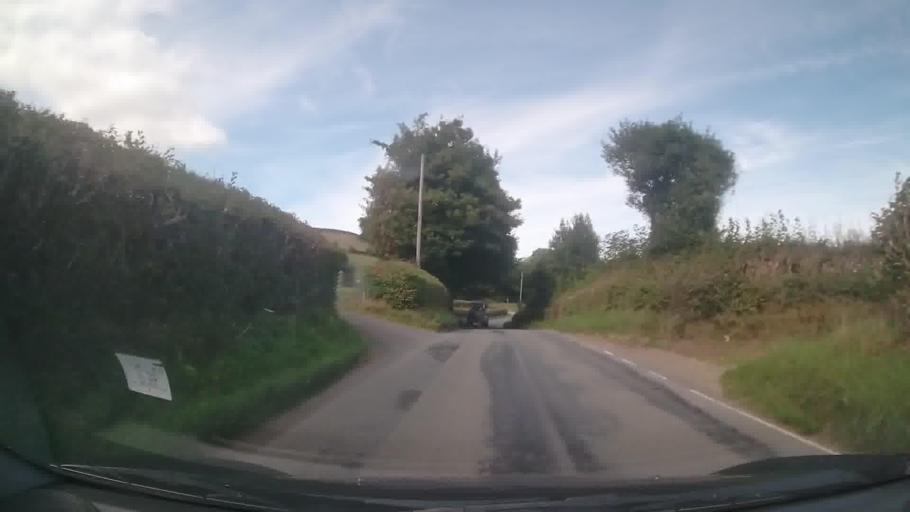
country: GB
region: Wales
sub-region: Sir Powys
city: Whitton
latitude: 52.2886
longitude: -3.0742
